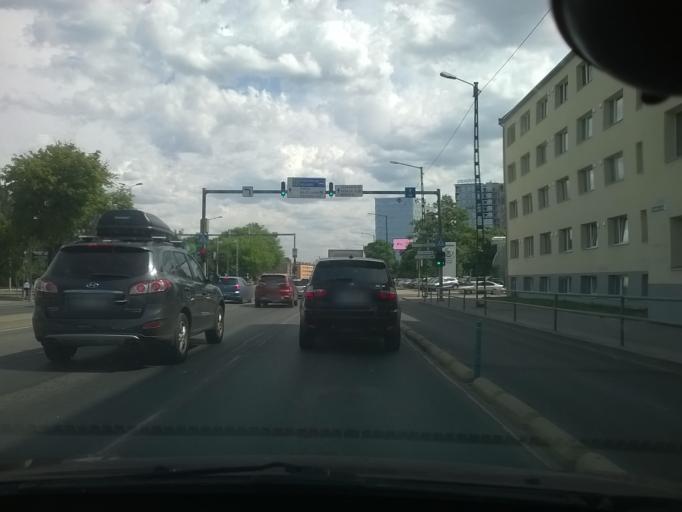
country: EE
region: Harju
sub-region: Tallinna linn
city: Tallinn
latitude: 59.4293
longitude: 24.6988
